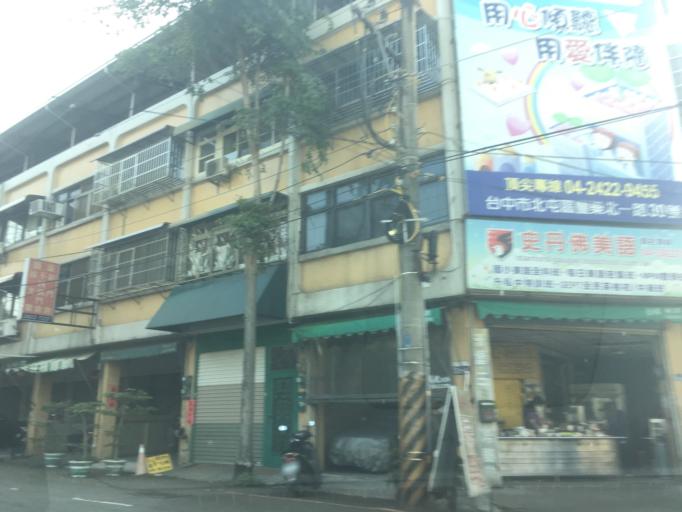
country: TW
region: Taiwan
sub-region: Taichung City
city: Taichung
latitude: 24.1941
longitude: 120.6820
